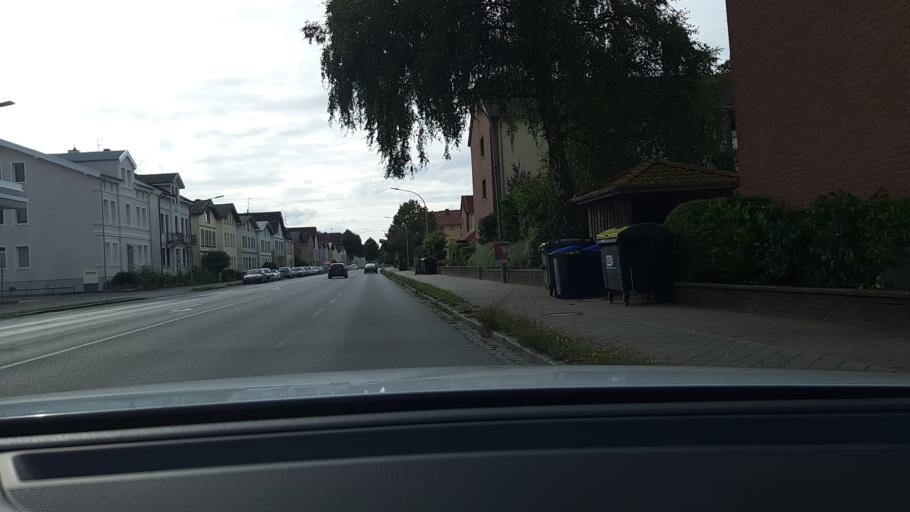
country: DE
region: Schleswig-Holstein
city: Stockelsdorf
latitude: 53.8879
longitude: 10.6452
